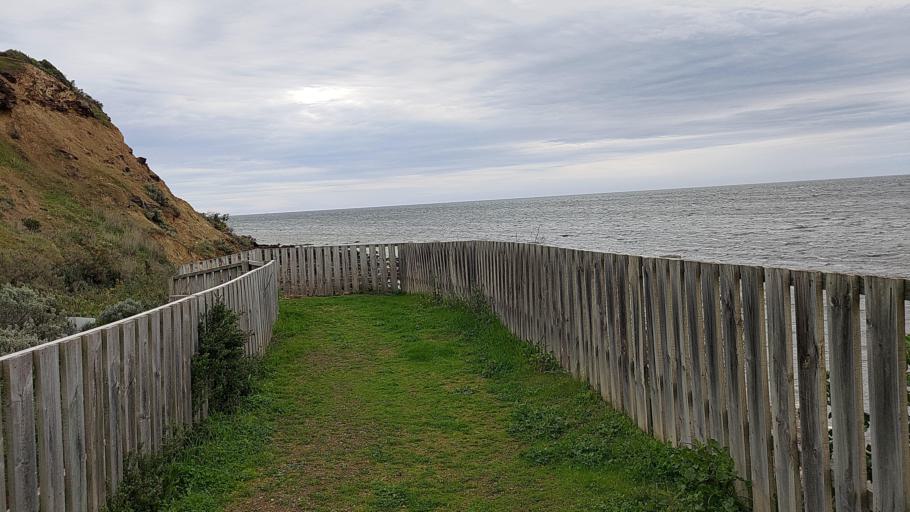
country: AU
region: South Australia
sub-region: Kangaroo Island
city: Kingscote
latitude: -35.6517
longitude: 137.6427
